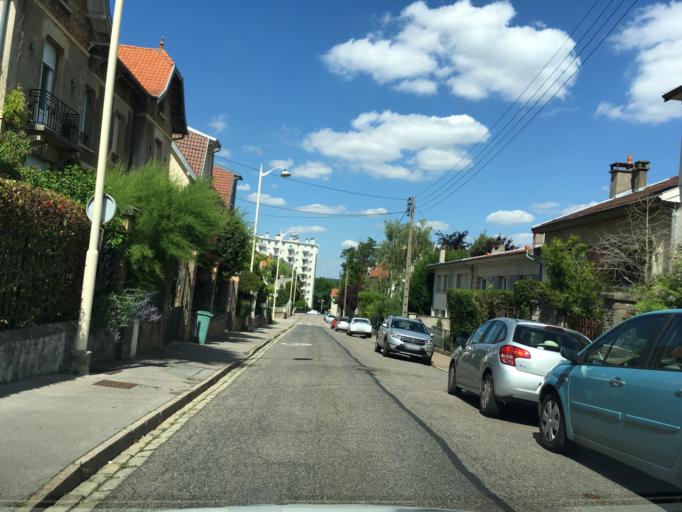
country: FR
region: Lorraine
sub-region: Departement de Meurthe-et-Moselle
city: Laxou
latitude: 48.6902
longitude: 6.1474
